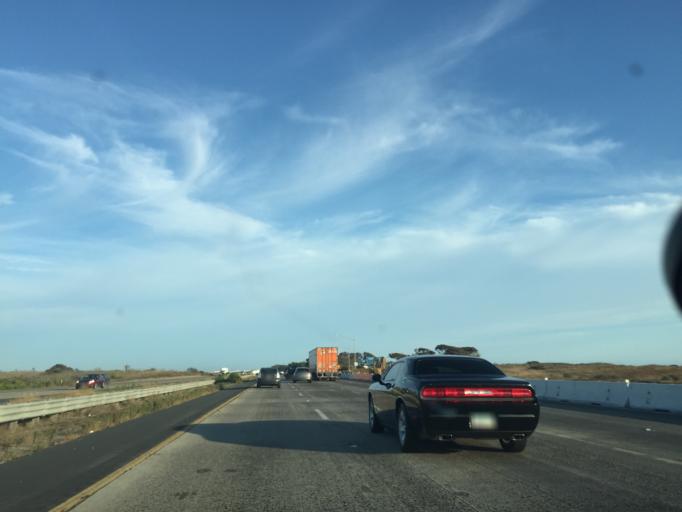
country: US
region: California
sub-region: San Diego County
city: Camp Pendleton South
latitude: 33.2774
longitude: -117.4464
